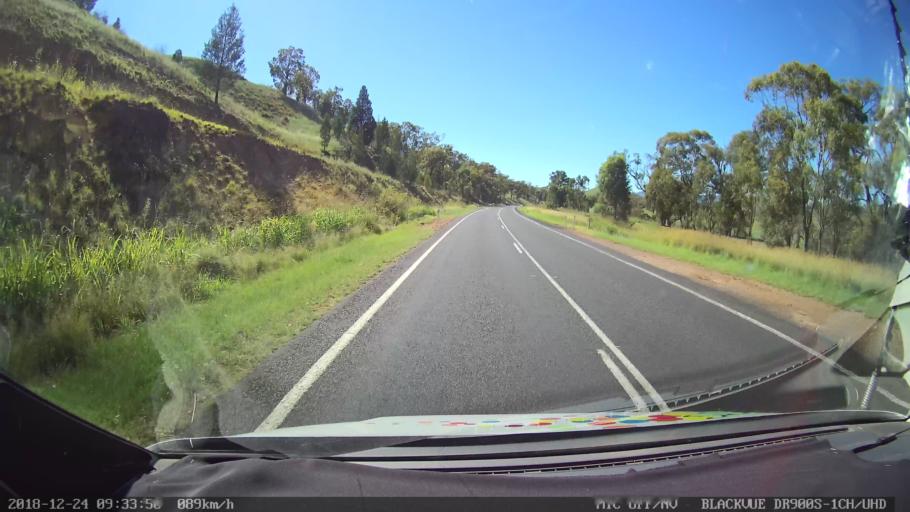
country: AU
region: New South Wales
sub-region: Liverpool Plains
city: Quirindi
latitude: -31.6074
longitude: 150.7112
